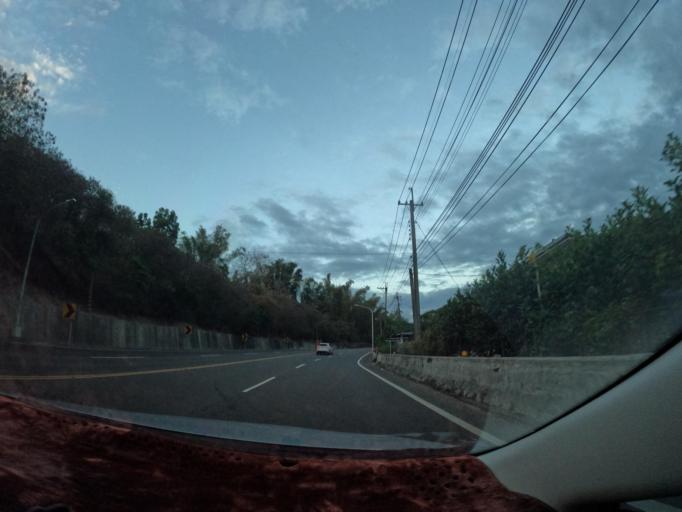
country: TW
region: Taiwan
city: Yujing
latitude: 23.0693
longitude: 120.4226
